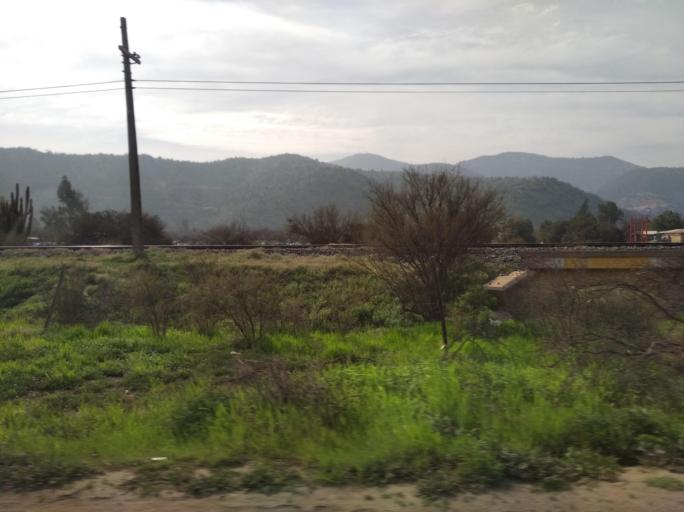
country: CL
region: Santiago Metropolitan
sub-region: Provincia de Chacabuco
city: Lampa
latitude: -33.1074
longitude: -70.9293
